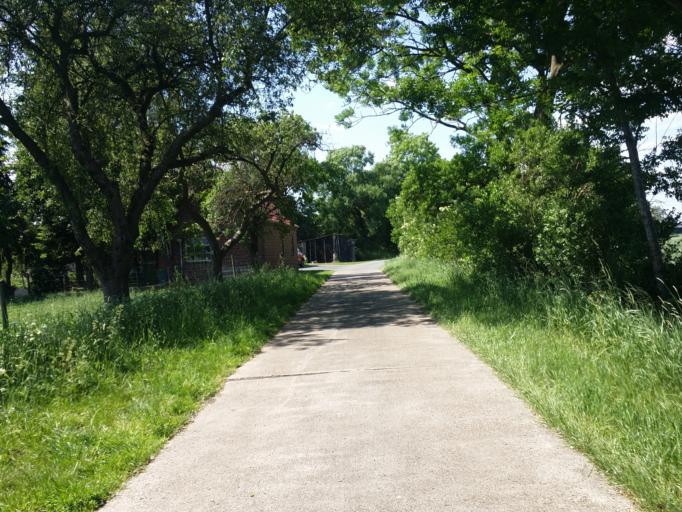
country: DE
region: Lower Saxony
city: Lemwerder
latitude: 53.1398
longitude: 8.5976
